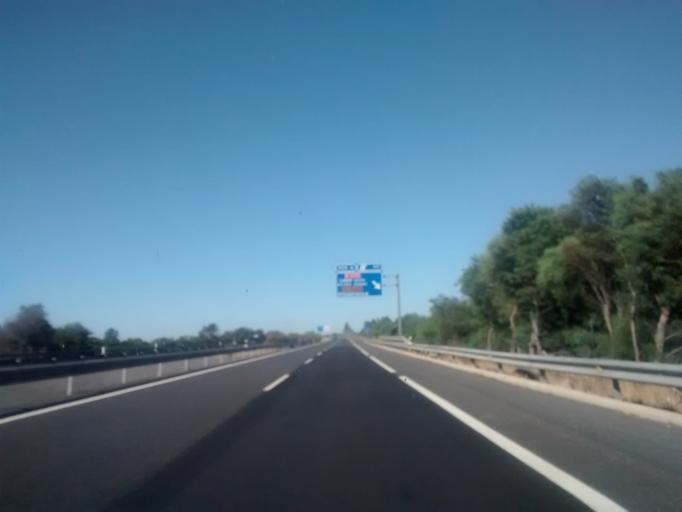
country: ES
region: Andalusia
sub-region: Provincia de Huelva
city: Lepe
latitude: 37.2829
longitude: -7.2416
